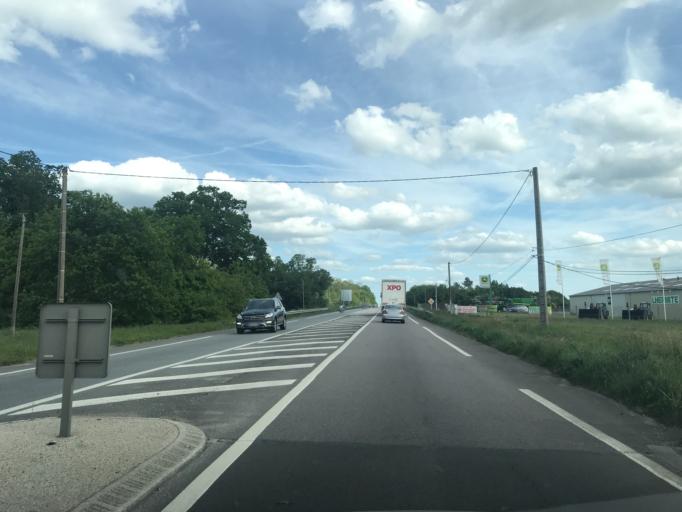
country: FR
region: Haute-Normandie
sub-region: Departement de l'Eure
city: Claville
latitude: 49.0651
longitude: 1.0286
